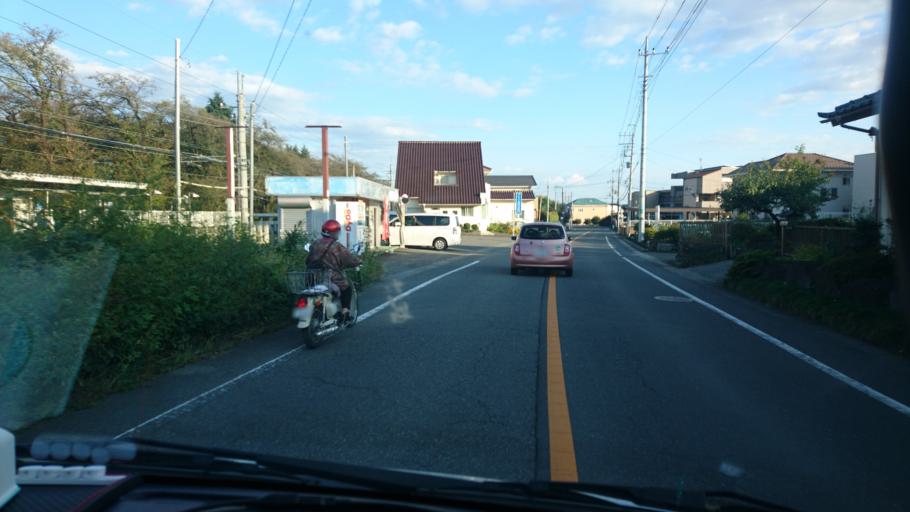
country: JP
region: Gunma
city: Omamacho-omama
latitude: 36.4194
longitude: 139.2975
